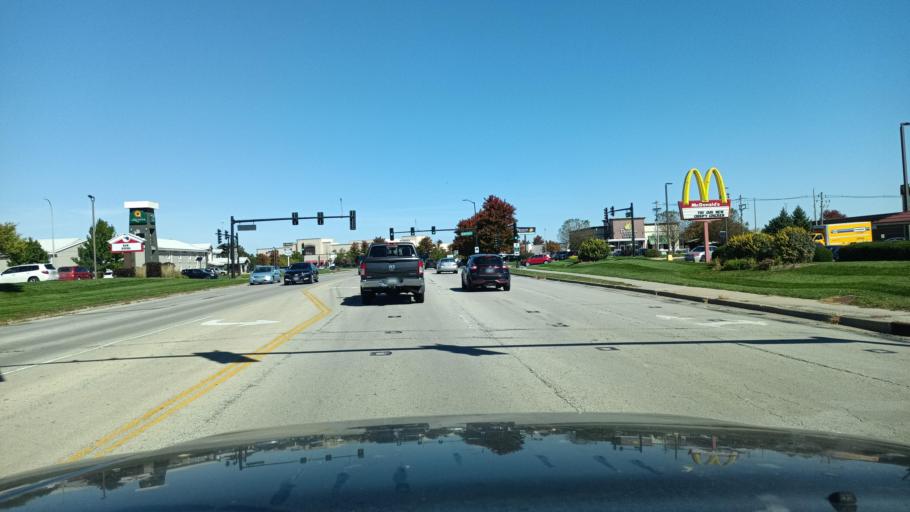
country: US
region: Illinois
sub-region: Champaign County
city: Champaign
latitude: 40.1371
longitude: -88.2437
